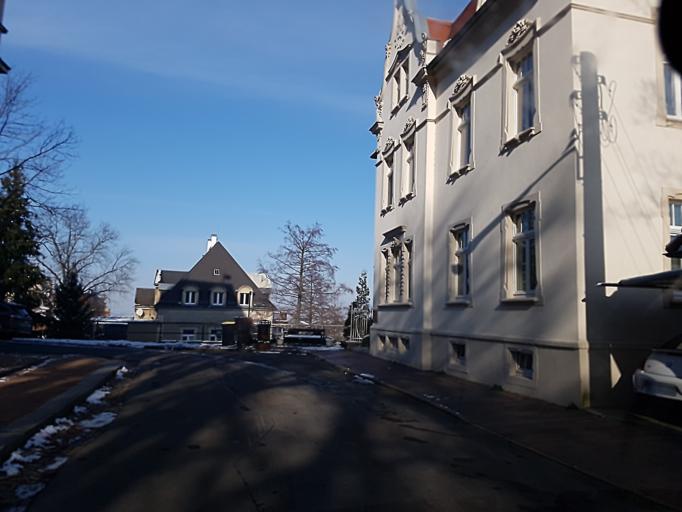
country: DE
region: Saxony
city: Leisnig
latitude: 51.1591
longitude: 12.9302
